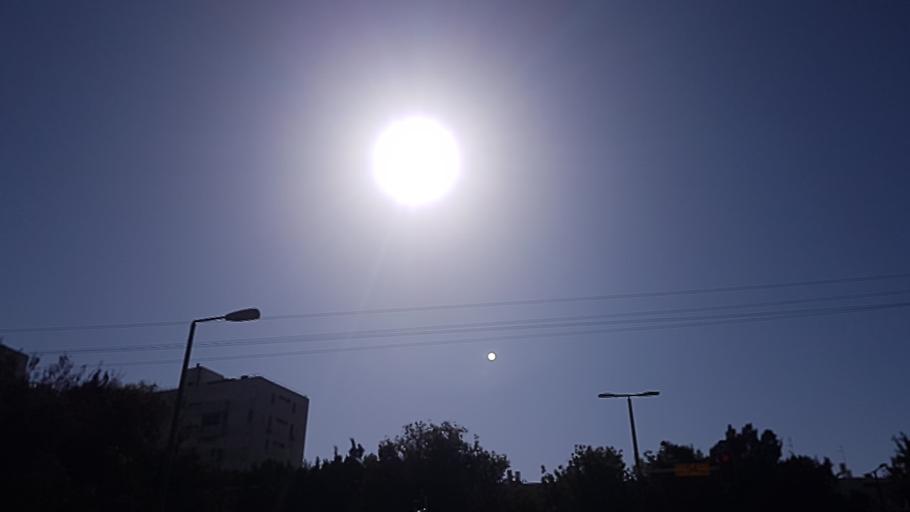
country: IL
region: Tel Aviv
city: Giv`atayim
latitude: 32.0614
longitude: 34.8209
